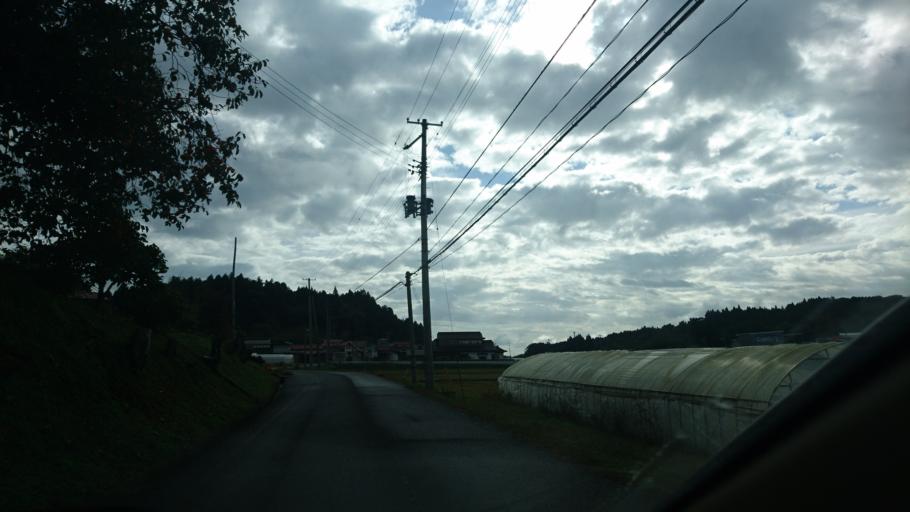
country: JP
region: Iwate
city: Ichinoseki
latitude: 38.7897
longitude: 140.9986
